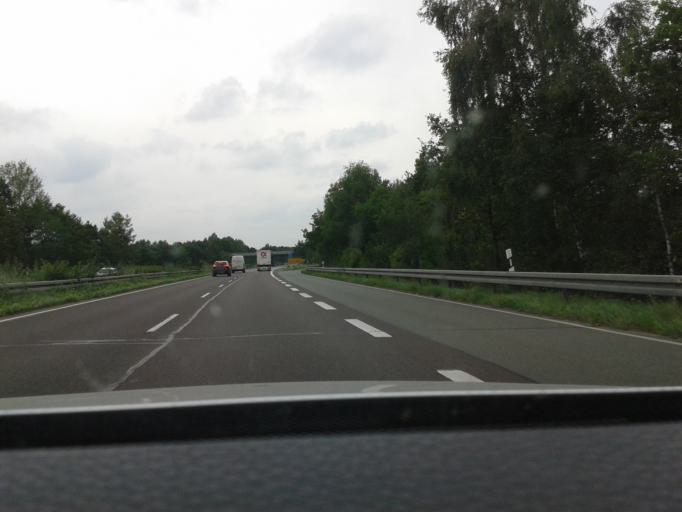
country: DE
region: Lower Saxony
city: Burgdorf
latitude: 52.4476
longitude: 9.9403
